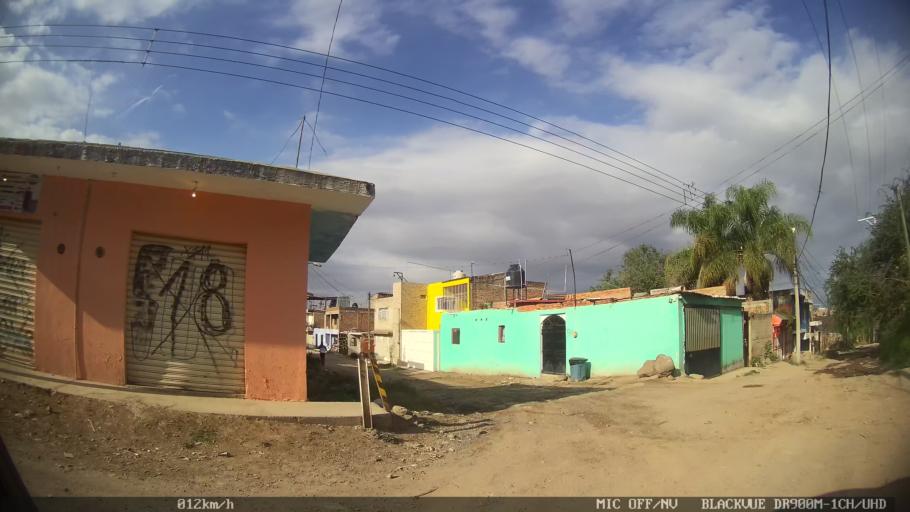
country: MX
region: Jalisco
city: Tonala
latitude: 20.6730
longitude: -103.2451
